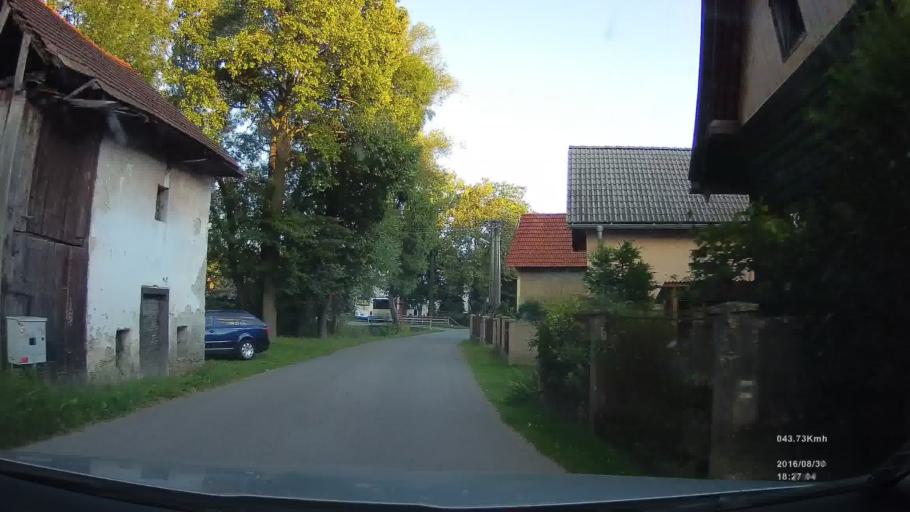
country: SK
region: Zilinsky
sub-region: Okres Liptovsky Mikulas
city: Liptovsky Mikulas
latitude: 49.1491
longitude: 19.5002
